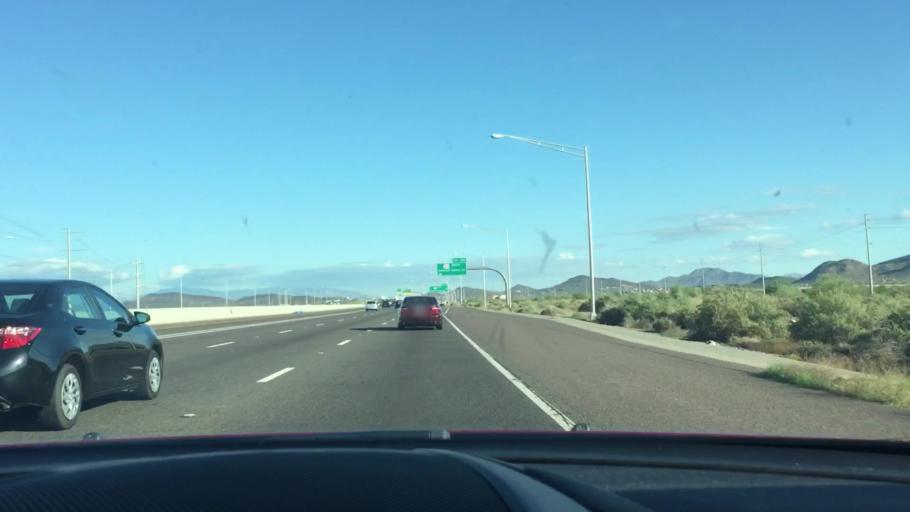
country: US
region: Arizona
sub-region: Maricopa County
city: Anthem
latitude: 33.7607
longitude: -112.1259
